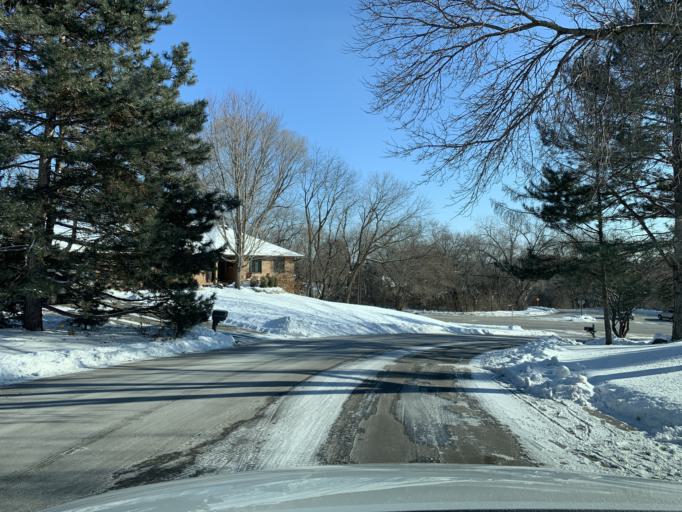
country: US
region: Minnesota
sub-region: Hennepin County
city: Bloomington
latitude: 44.8368
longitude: -93.3466
